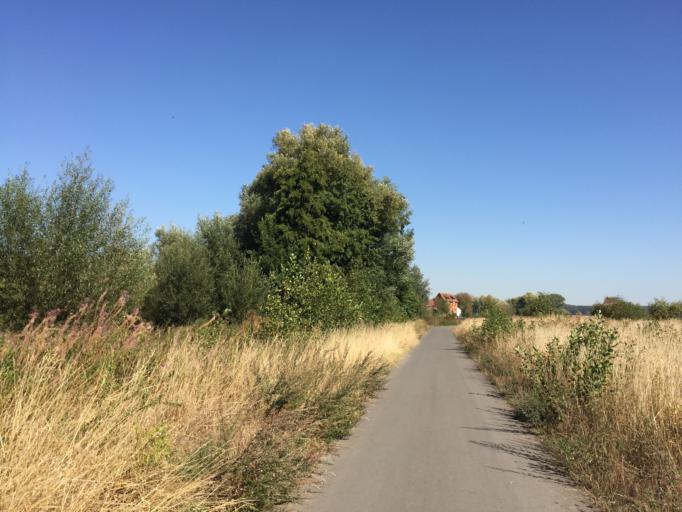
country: DE
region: Hesse
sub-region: Regierungsbezirk Giessen
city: Hungen
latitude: 50.4506
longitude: 8.9131
